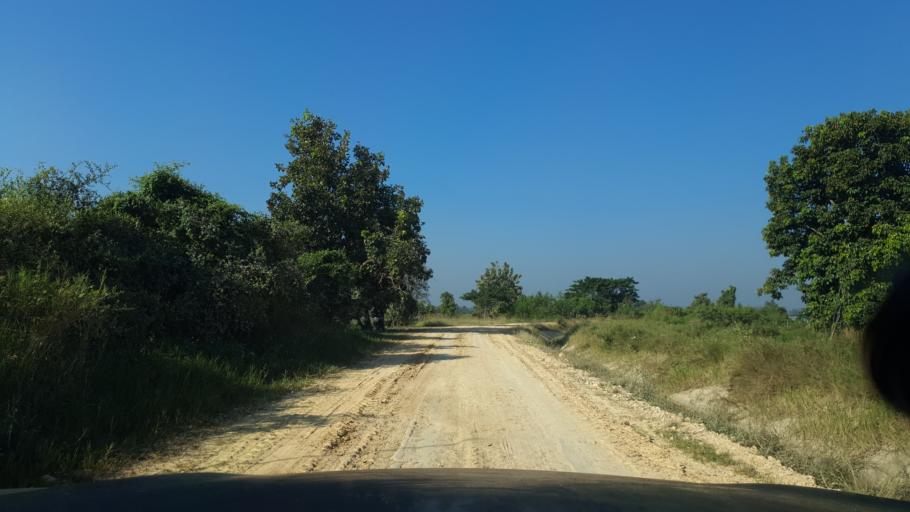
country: TH
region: Chiang Mai
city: San Kamphaeng
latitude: 18.7037
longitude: 99.1345
